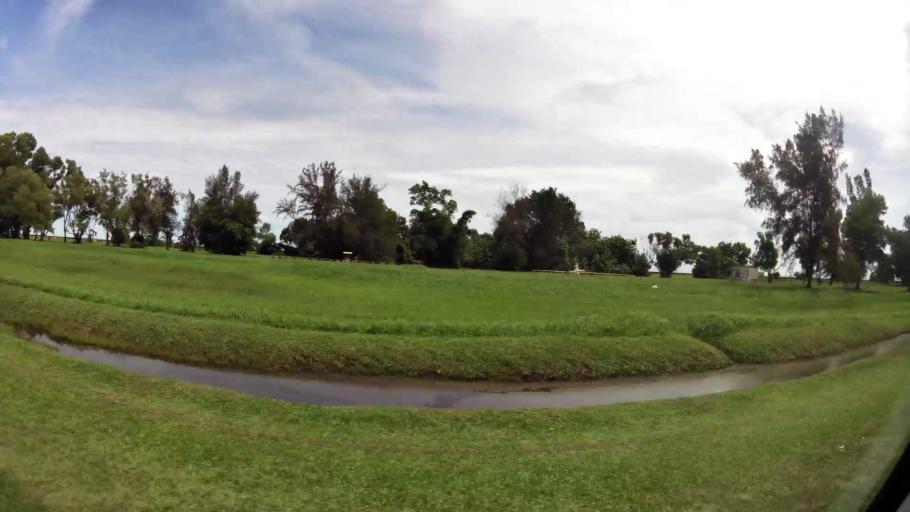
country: BN
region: Belait
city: Seria
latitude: 4.6097
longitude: 114.3000
